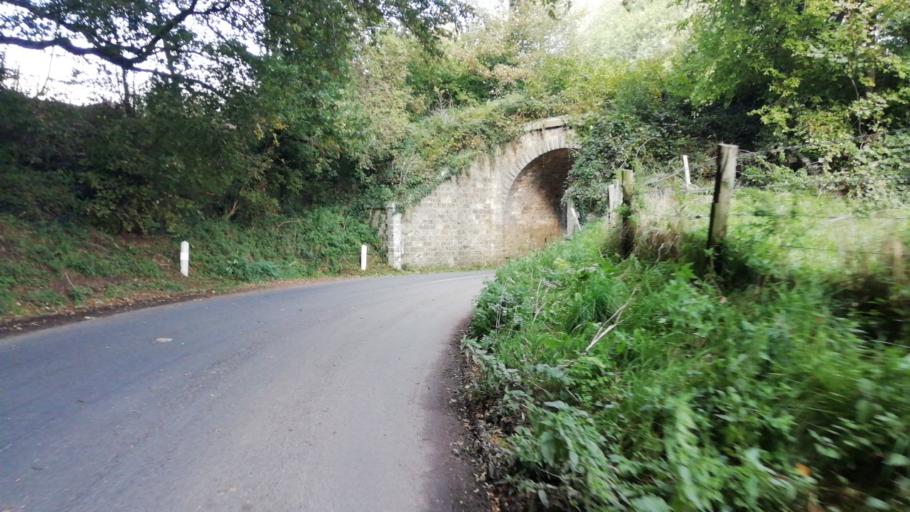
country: FR
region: Haute-Normandie
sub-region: Departement de la Seine-Maritime
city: Rolleville
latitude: 49.5975
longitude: 0.2120
